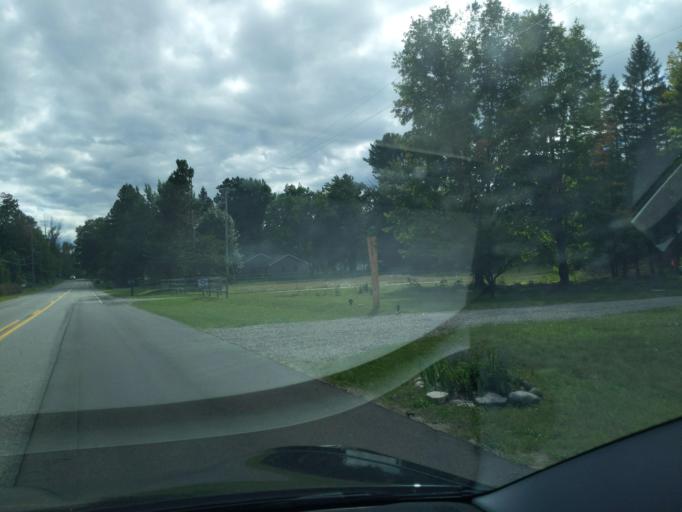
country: US
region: Michigan
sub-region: Kalkaska County
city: Rapid City
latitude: 44.9253
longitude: -85.2857
